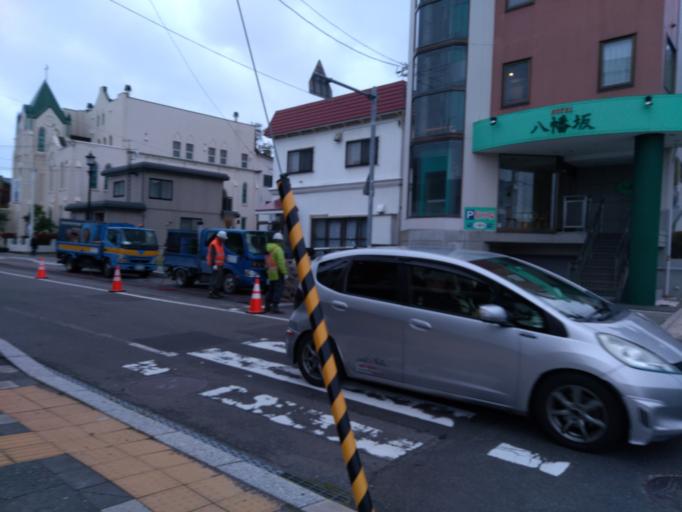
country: JP
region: Hokkaido
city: Hakodate
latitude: 41.7652
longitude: 140.7133
